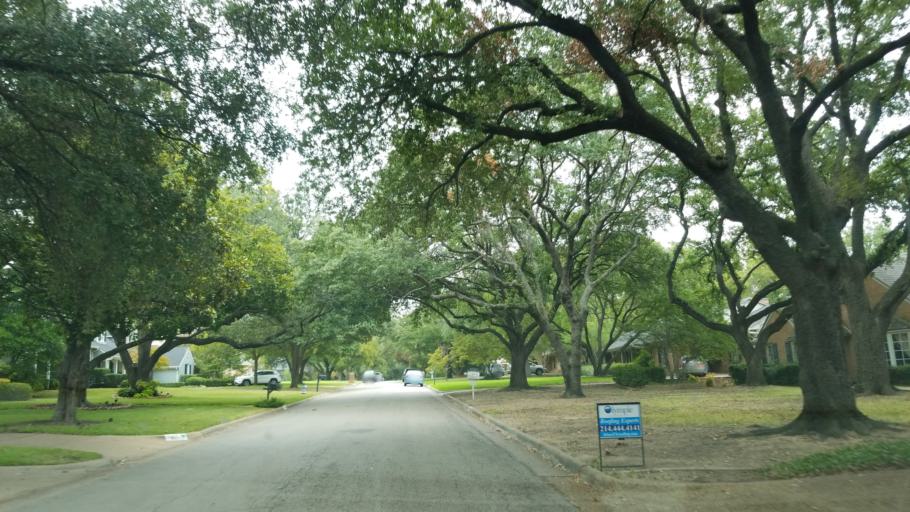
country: US
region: Texas
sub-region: Dallas County
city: Richardson
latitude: 32.9411
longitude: -96.7769
